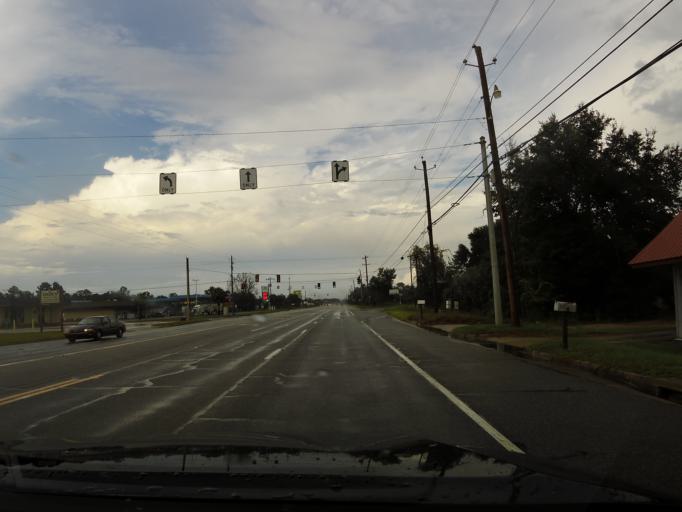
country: US
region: Georgia
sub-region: Wayne County
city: Jesup
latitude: 31.6470
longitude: -81.8559
